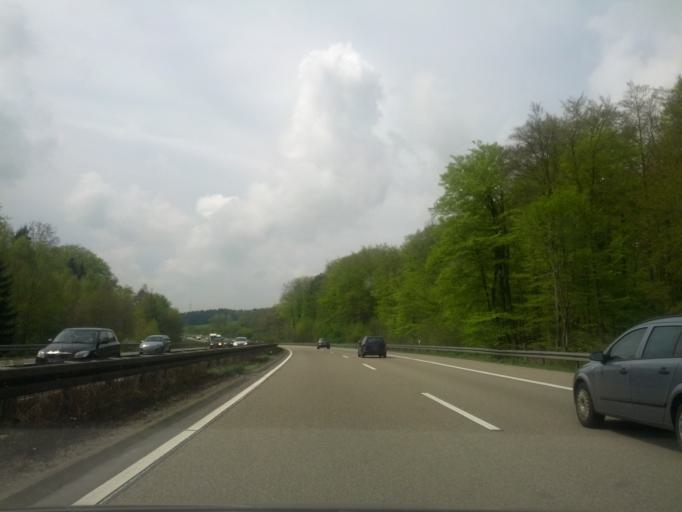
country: DE
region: Hesse
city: Kirtorf
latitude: 50.7165
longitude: 9.0779
